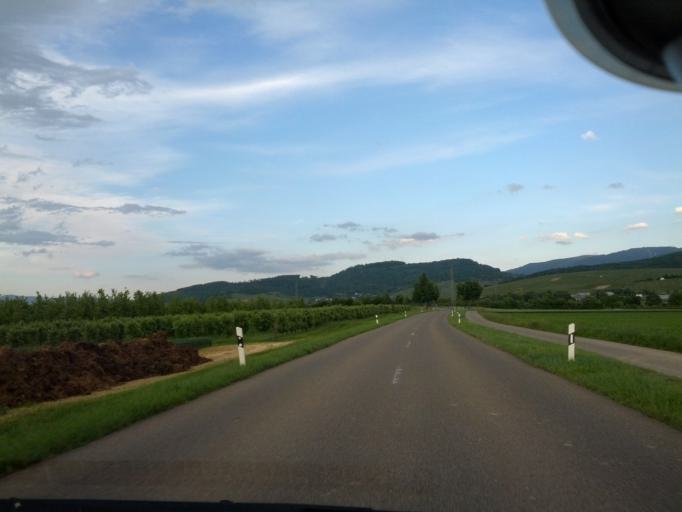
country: DE
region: Baden-Wuerttemberg
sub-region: Freiburg Region
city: Schallstadt
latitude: 47.9557
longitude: 7.7317
